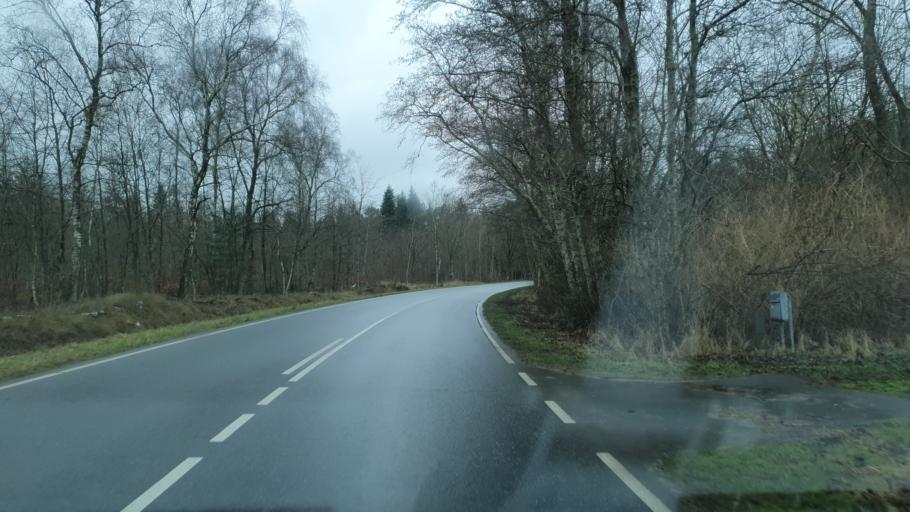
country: DK
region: North Denmark
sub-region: Jammerbugt Kommune
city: Fjerritslev
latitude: 57.1187
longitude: 9.1259
